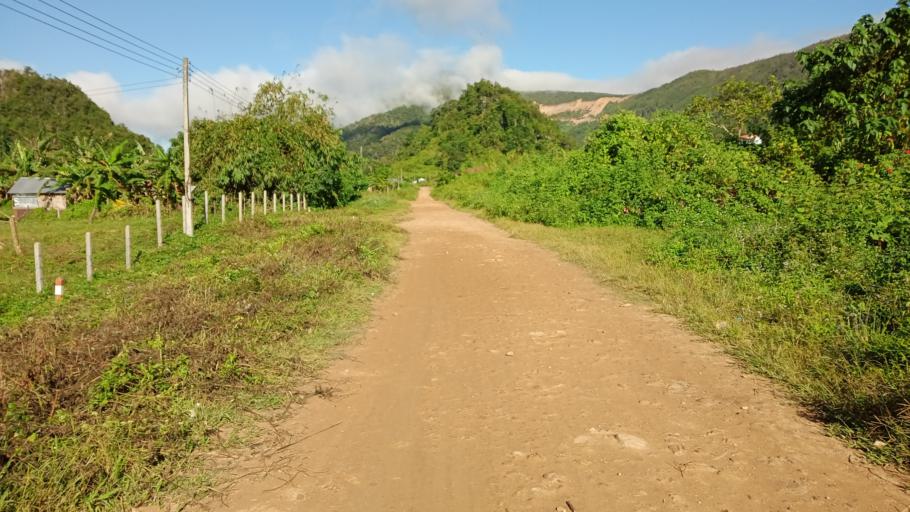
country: LA
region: Xiangkhoang
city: Phonsavan
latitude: 19.1144
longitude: 102.9128
